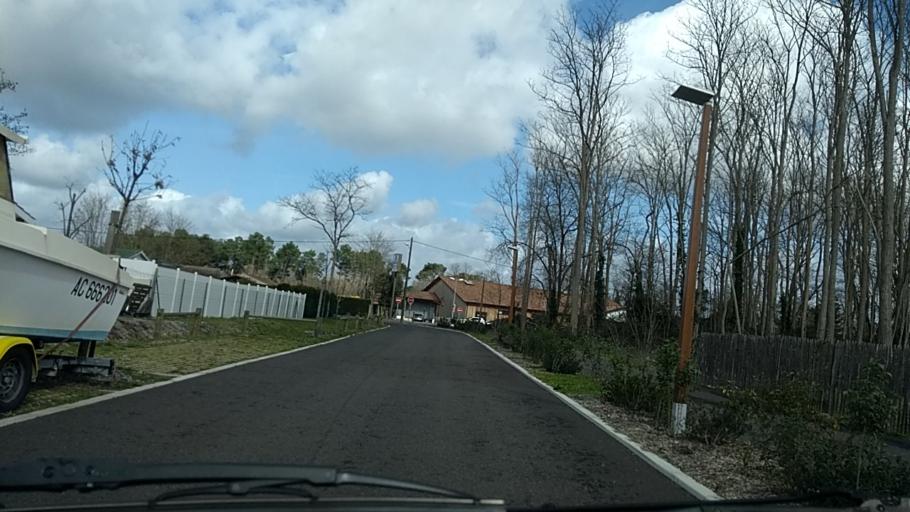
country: FR
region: Aquitaine
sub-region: Departement de la Gironde
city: Salles
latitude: 44.5472
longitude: -0.8776
